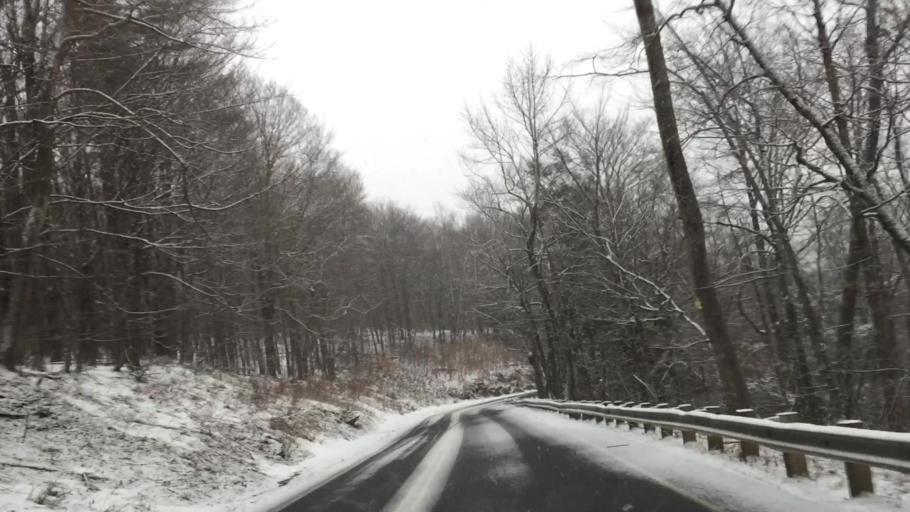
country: US
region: Massachusetts
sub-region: Berkshire County
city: Hinsdale
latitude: 42.4134
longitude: -73.1823
